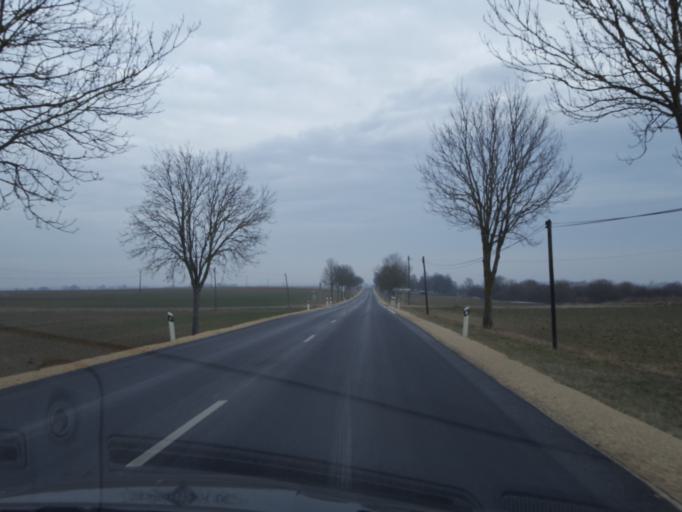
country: FR
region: Lorraine
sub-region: Departement de la Meuse
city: Etain
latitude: 49.2009
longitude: 5.5549
